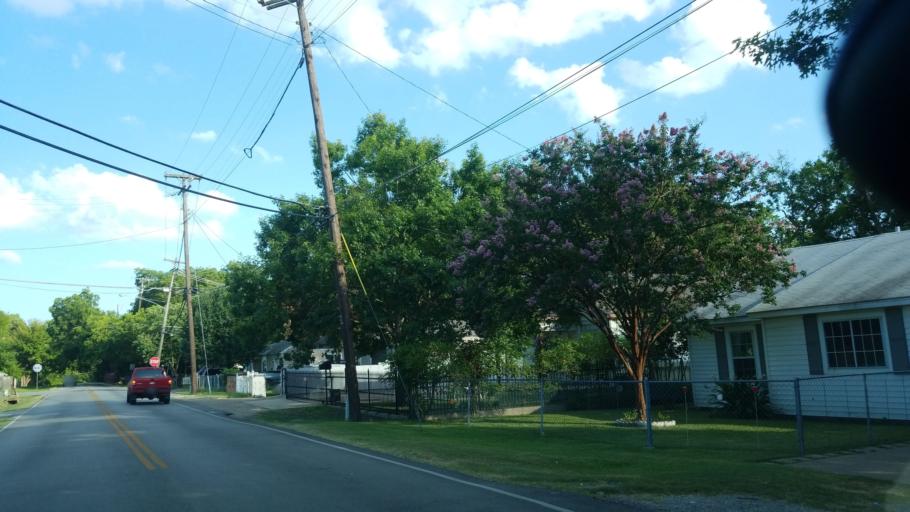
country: US
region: Texas
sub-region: Dallas County
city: Dallas
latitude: 32.7835
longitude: -96.7172
